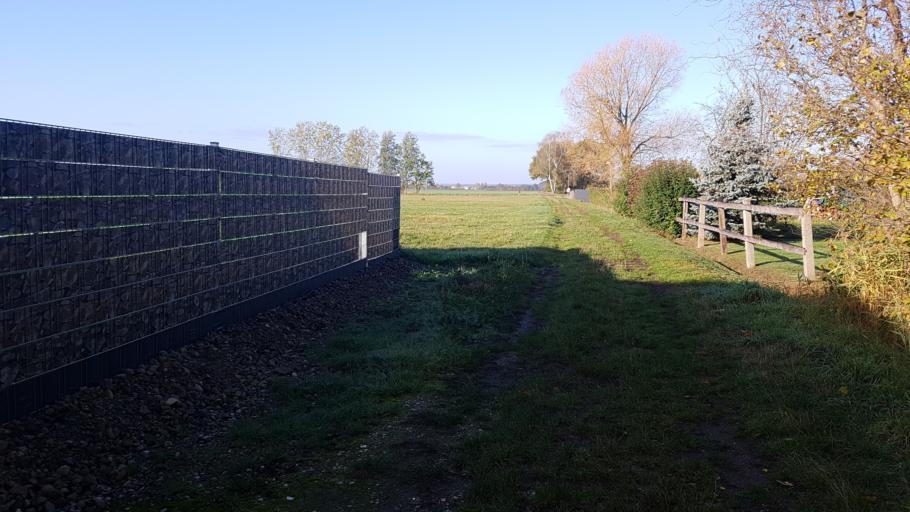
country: DE
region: Brandenburg
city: Ruckersdorf
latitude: 51.5738
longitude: 13.5665
